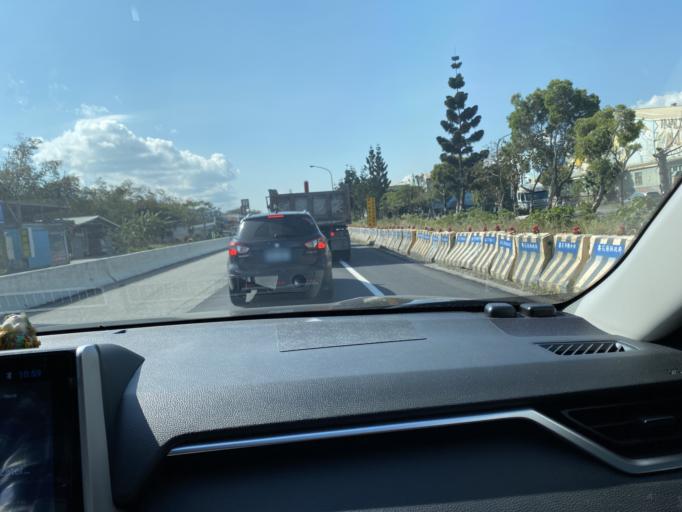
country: TW
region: Taiwan
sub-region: Hualien
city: Hualian
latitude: 23.9290
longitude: 121.5929
